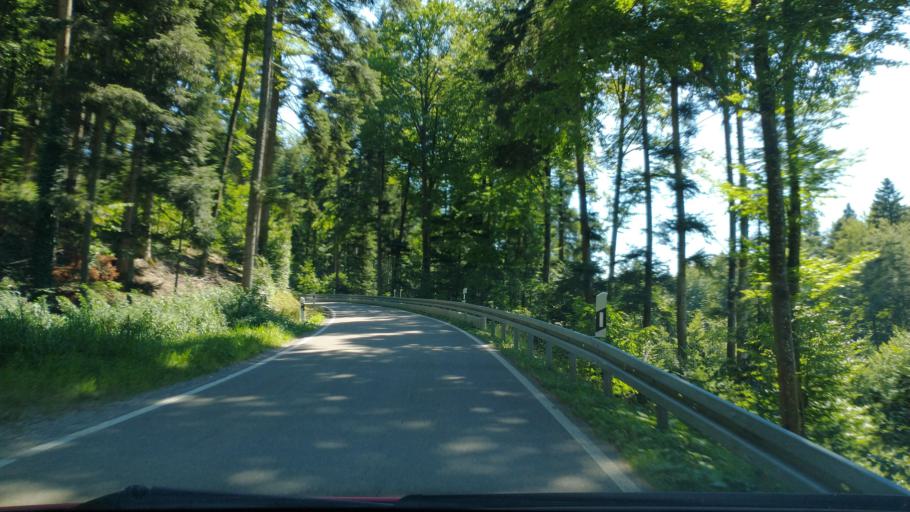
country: DE
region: Baden-Wuerttemberg
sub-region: Regierungsbezirk Stuttgart
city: Welzheim
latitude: 48.8473
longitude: 9.6252
